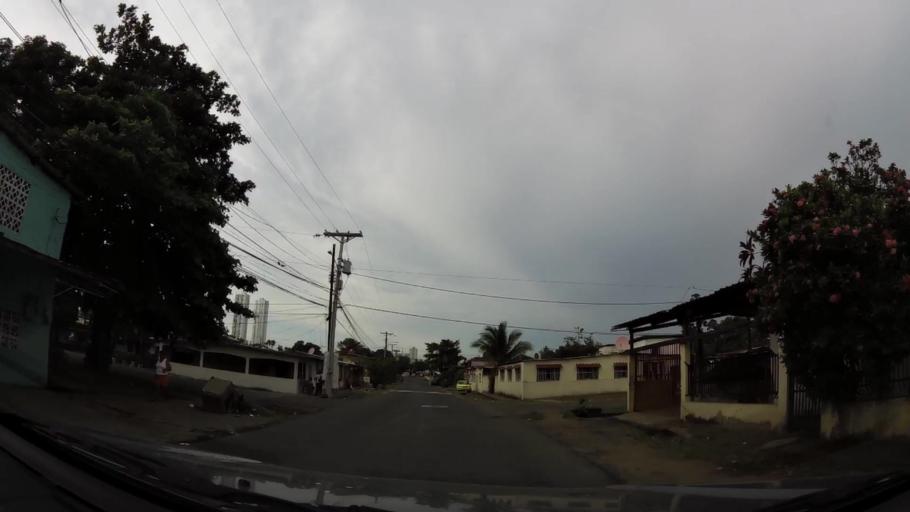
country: PA
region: Panama
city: Panama
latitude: 9.0087
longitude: -79.4897
